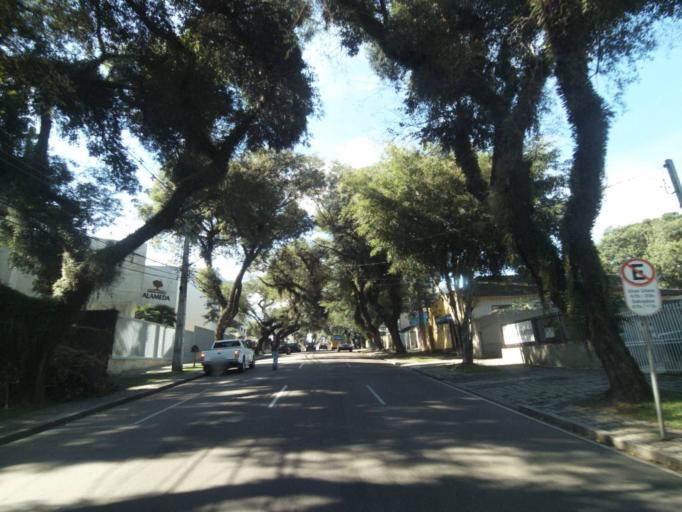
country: BR
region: Parana
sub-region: Curitiba
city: Curitiba
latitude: -25.4361
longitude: -49.2984
